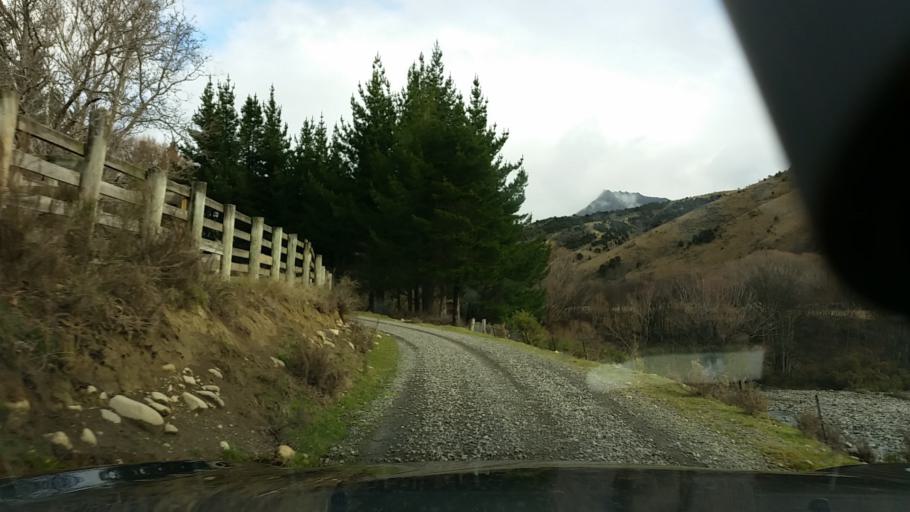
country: NZ
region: Tasman
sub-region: Tasman District
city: Brightwater
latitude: -41.7370
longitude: 173.4196
